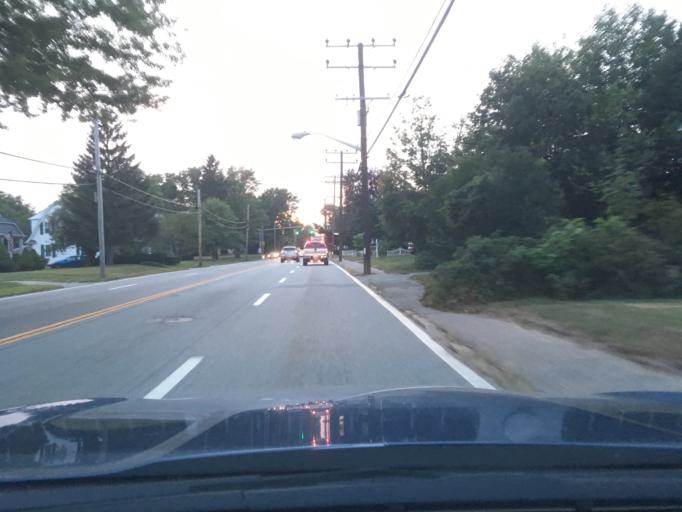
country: US
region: Rhode Island
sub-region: Kent County
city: Warwick
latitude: 41.7124
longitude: -71.4509
